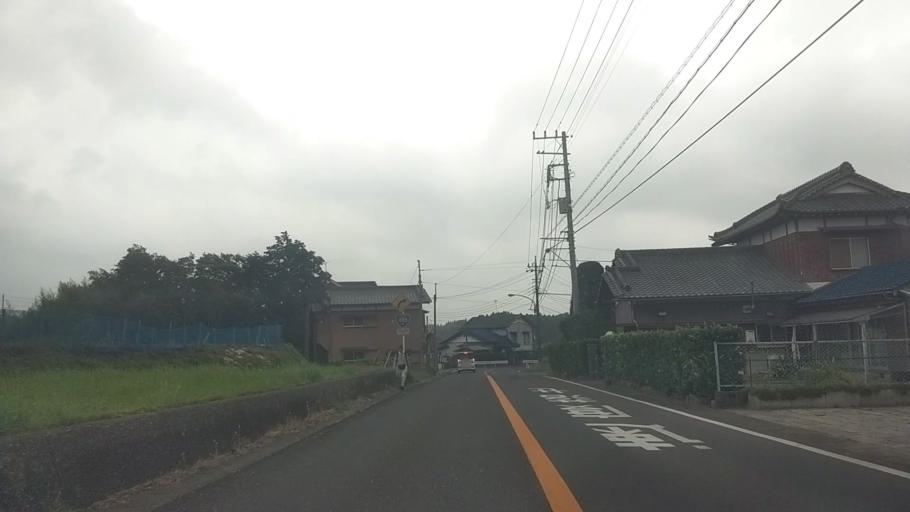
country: JP
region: Chiba
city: Ohara
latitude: 35.2804
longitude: 140.3245
